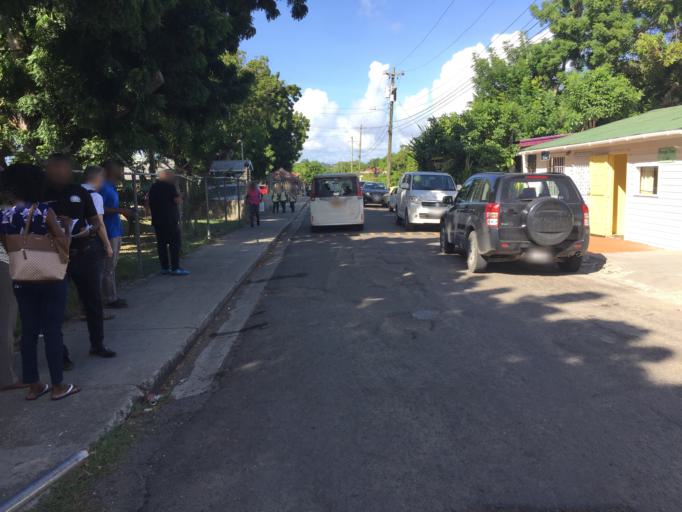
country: AG
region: Saint John
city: Saint John's
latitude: 17.1259
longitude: -61.8418
